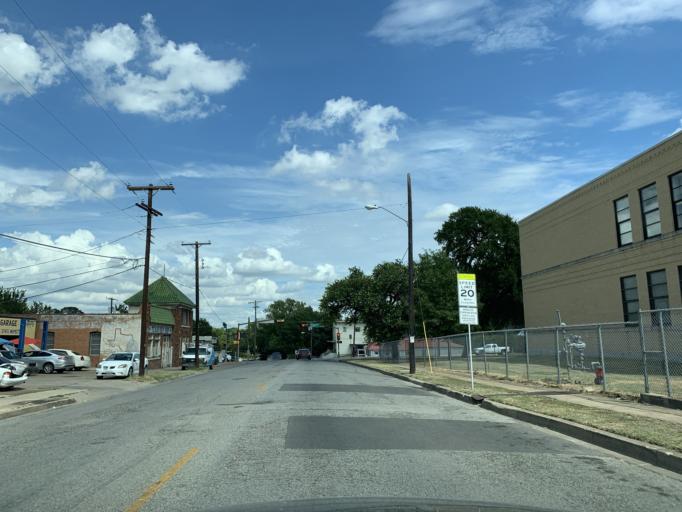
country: US
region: Texas
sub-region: Dallas County
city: Cockrell Hill
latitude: 32.7350
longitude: -96.8452
